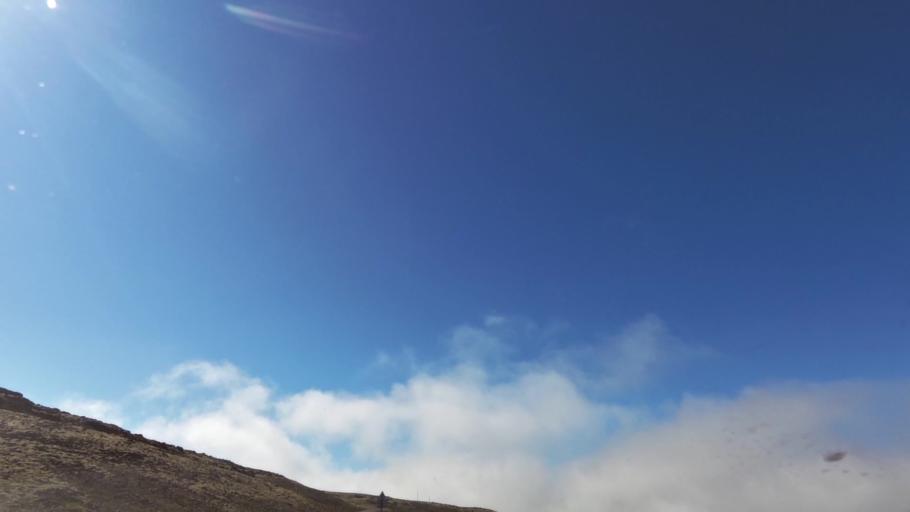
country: IS
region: West
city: Olafsvik
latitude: 65.5526
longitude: -24.2203
